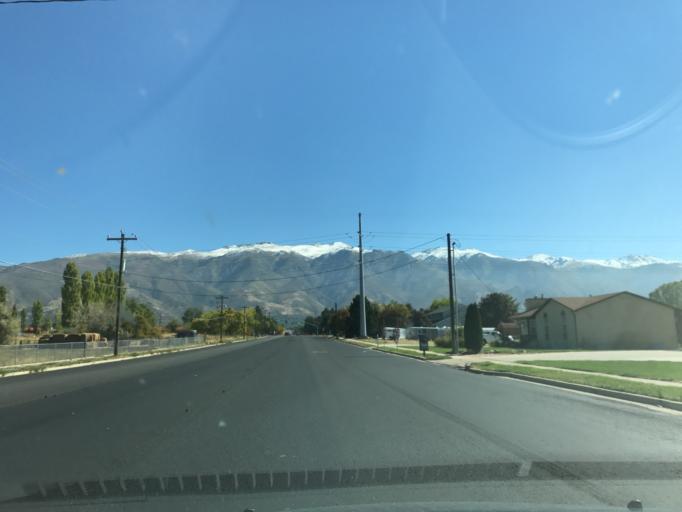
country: US
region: Utah
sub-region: Davis County
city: Hill Air Force Bace
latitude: 41.0889
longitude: -111.9534
